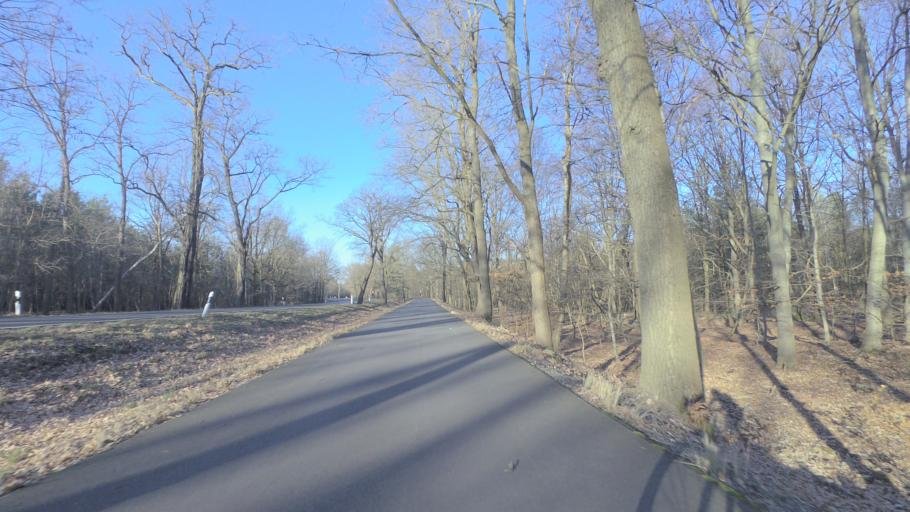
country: DE
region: Brandenburg
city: Sperenberg
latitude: 52.0216
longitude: 13.3190
